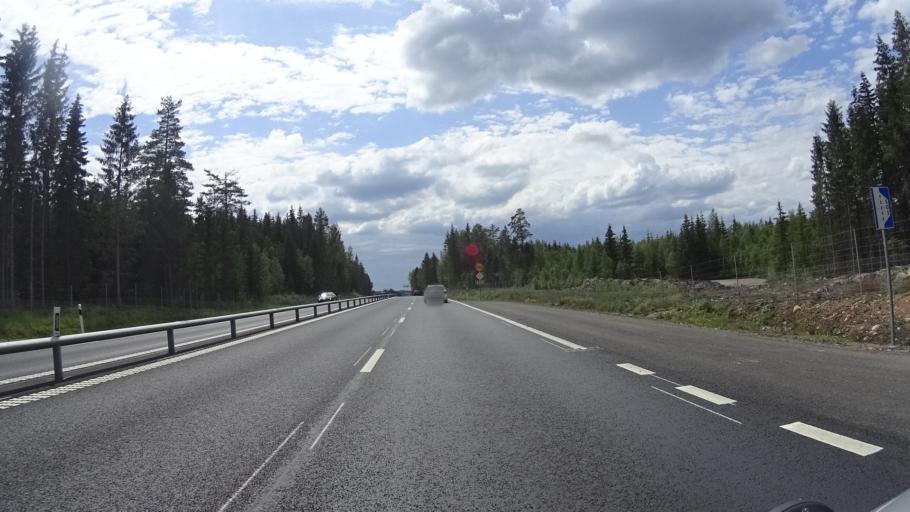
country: SE
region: Vaestra Goetaland
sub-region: Gullspangs Kommun
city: Hova
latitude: 58.8333
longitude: 14.1789
